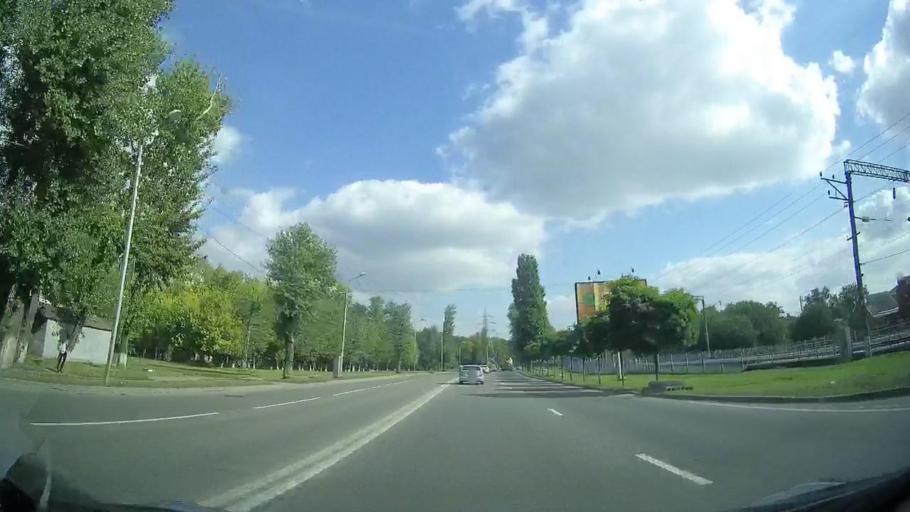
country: RU
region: Rostov
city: Imeni Chkalova
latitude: 47.2601
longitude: 39.7881
